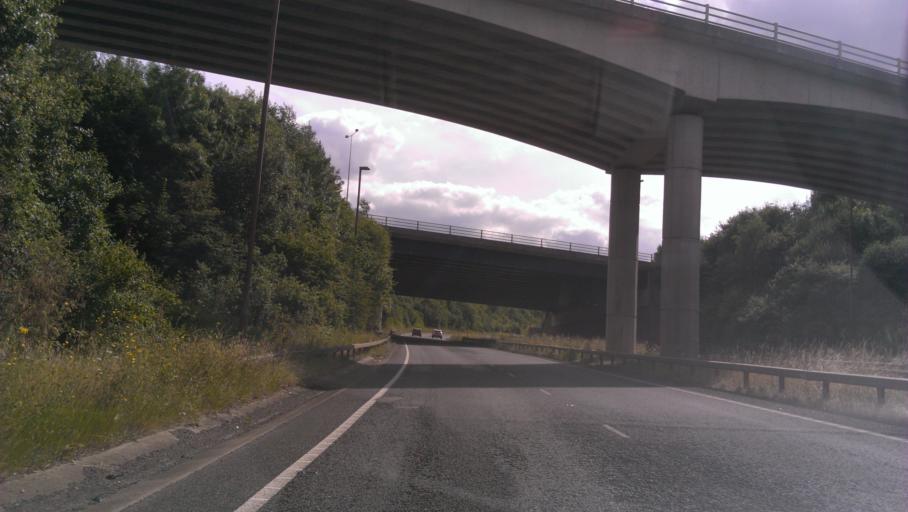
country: GB
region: England
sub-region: Medway
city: Cuxton
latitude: 51.4007
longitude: 0.4463
